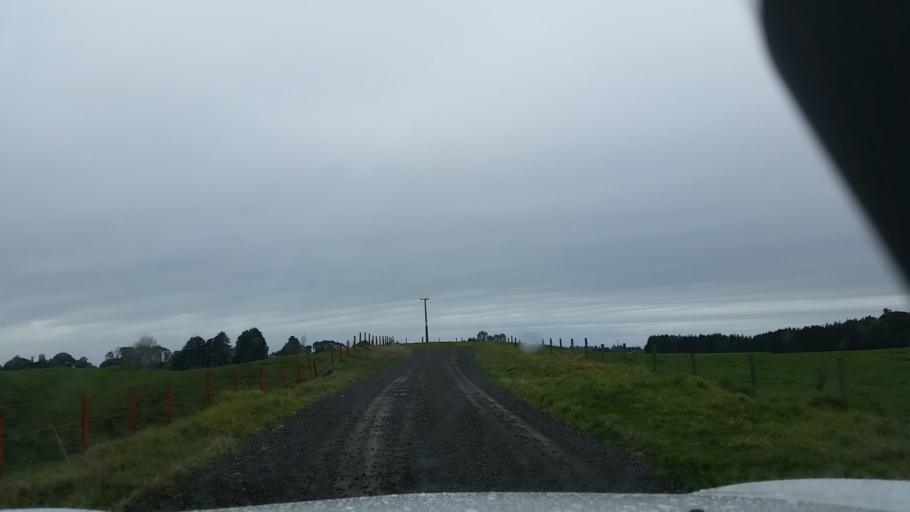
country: NZ
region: Bay of Plenty
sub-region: Western Bay of Plenty District
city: Maketu
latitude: -37.9660
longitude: 176.4348
